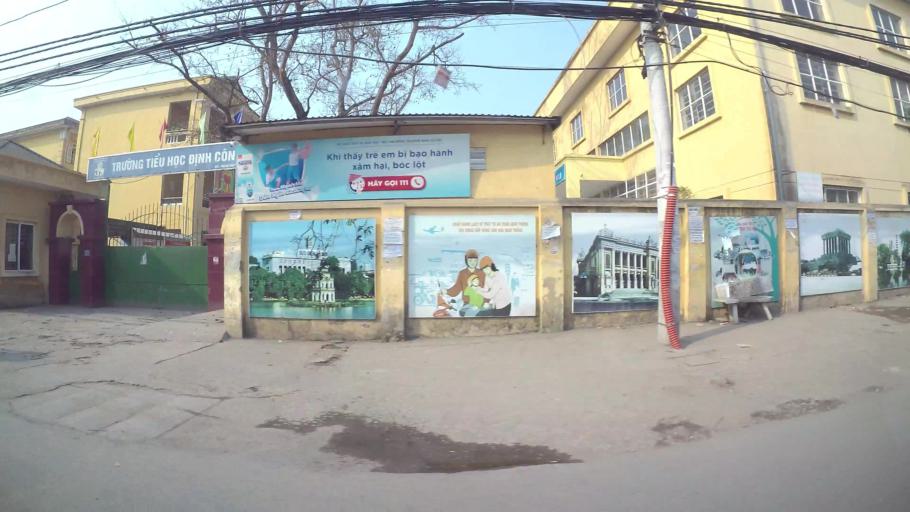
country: VN
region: Ha Noi
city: Thanh Xuan
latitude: 20.9830
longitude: 105.8267
